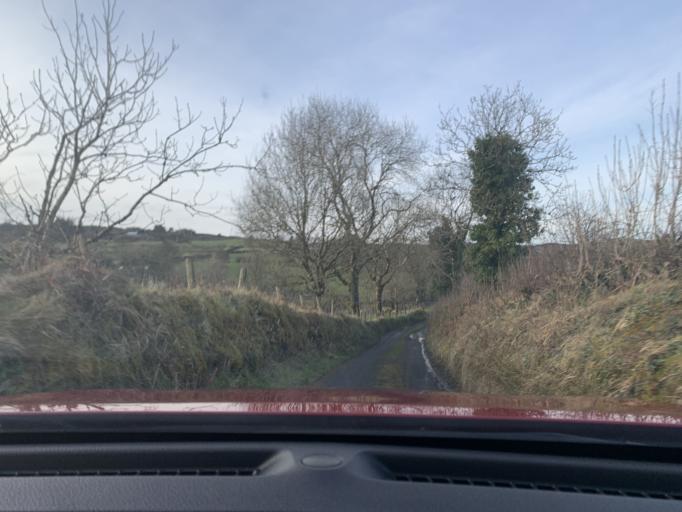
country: IE
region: Connaught
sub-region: Sligo
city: Strandhill
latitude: 54.1700
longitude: -8.6549
